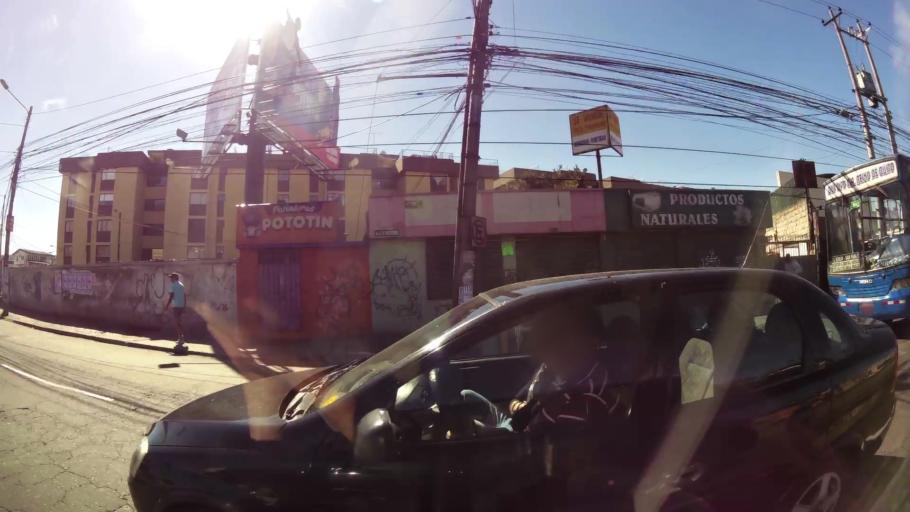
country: EC
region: Pichincha
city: Quito
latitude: -0.1551
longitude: -78.4769
